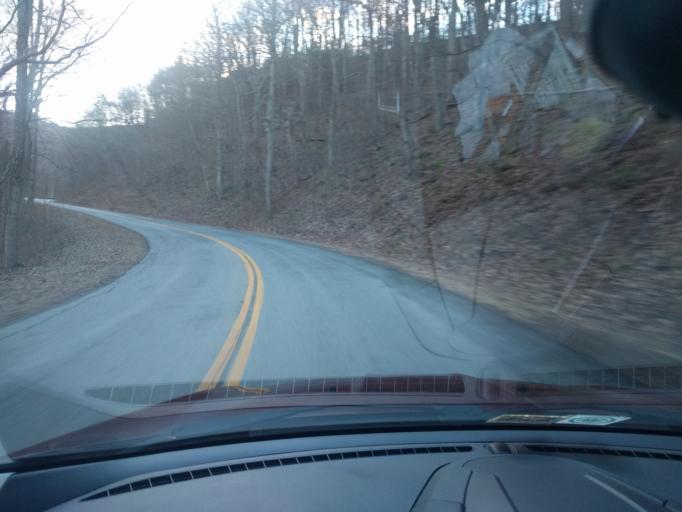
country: US
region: Virginia
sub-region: Botetourt County
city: Buchanan
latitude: 37.4653
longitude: -79.6362
